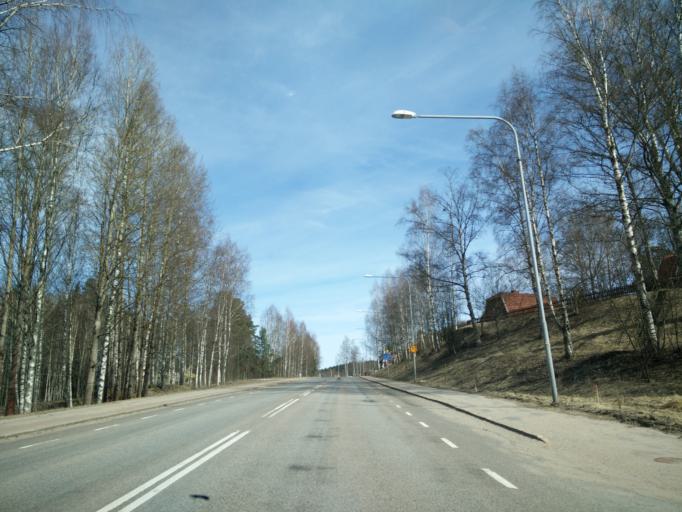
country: SE
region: Vaermland
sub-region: Hagfors Kommun
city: Hagfors
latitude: 60.0219
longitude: 13.6947
